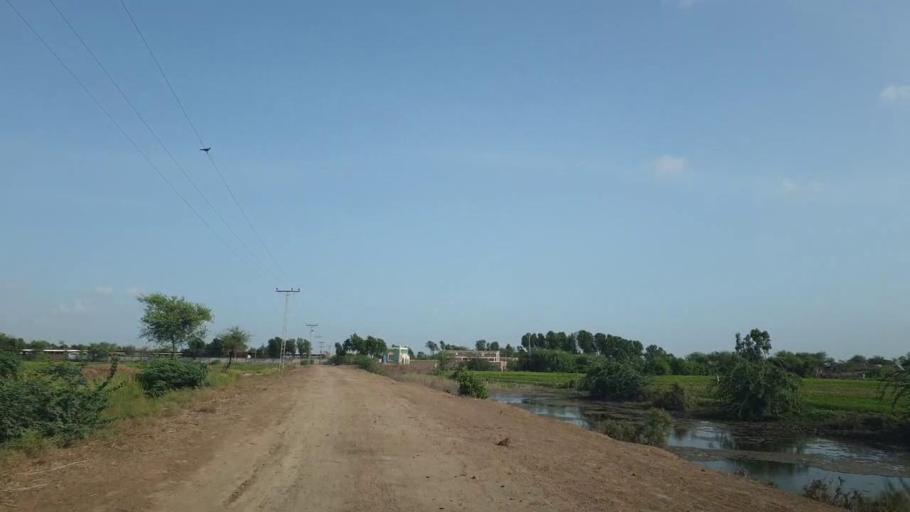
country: PK
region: Sindh
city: Kadhan
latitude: 24.6244
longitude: 69.0850
